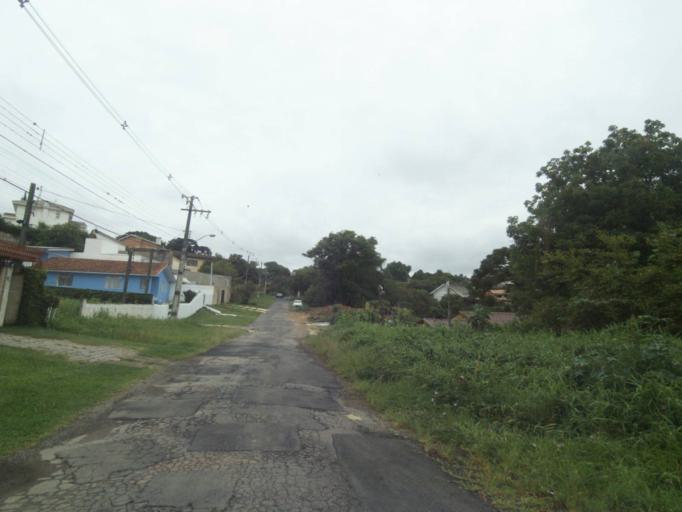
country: BR
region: Parana
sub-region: Curitiba
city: Curitiba
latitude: -25.4092
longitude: -49.2884
